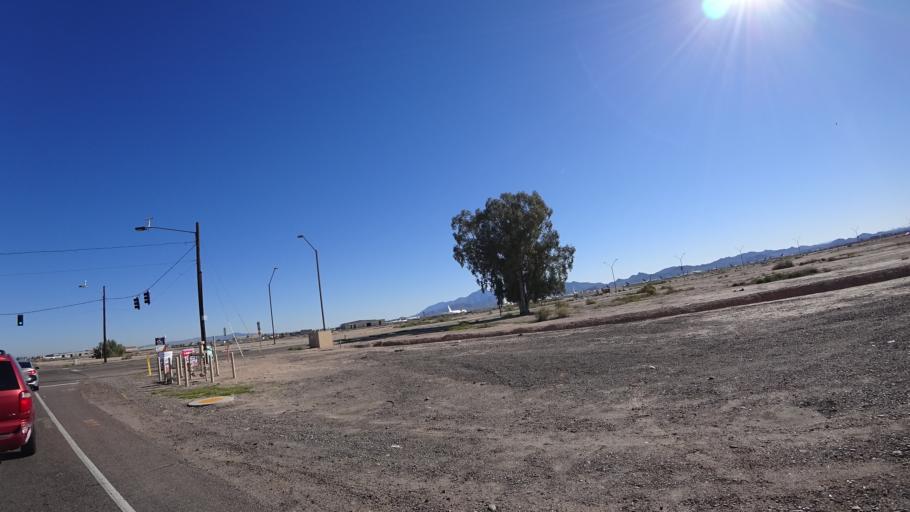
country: US
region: Arizona
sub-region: Maricopa County
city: Goodyear
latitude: 33.4355
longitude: -112.3762
